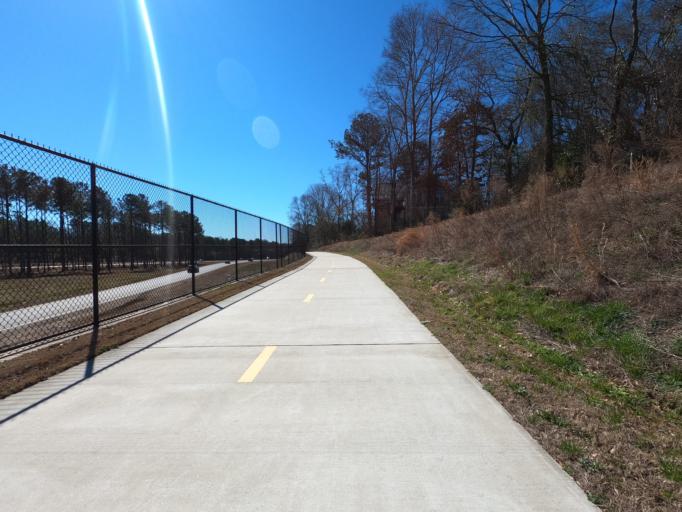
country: US
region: Georgia
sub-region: Clarke County
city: Athens
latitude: 33.9466
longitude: -83.3591
